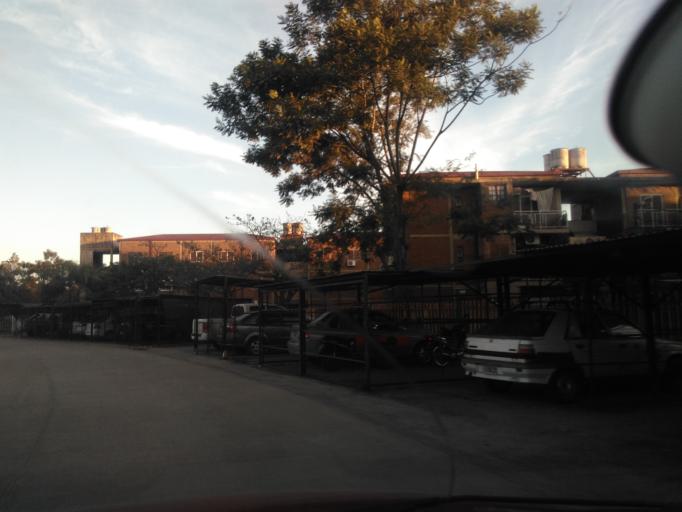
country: AR
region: Chaco
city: Resistencia
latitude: -27.4764
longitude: -58.9880
